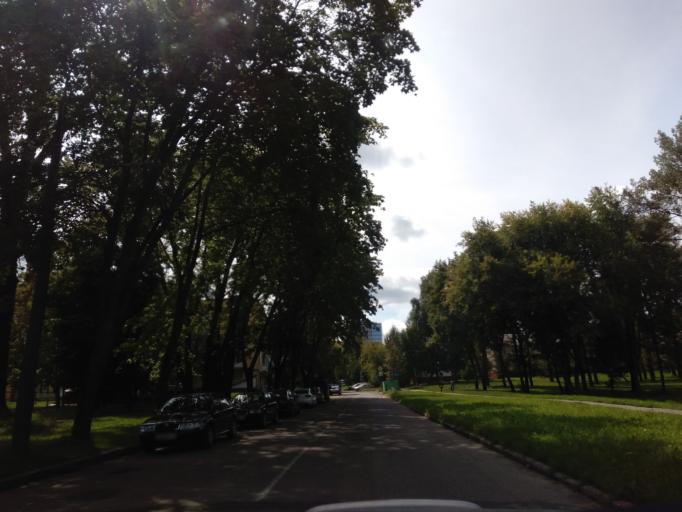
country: BY
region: Minsk
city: Novoye Medvezhino
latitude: 53.8780
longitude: 27.5039
